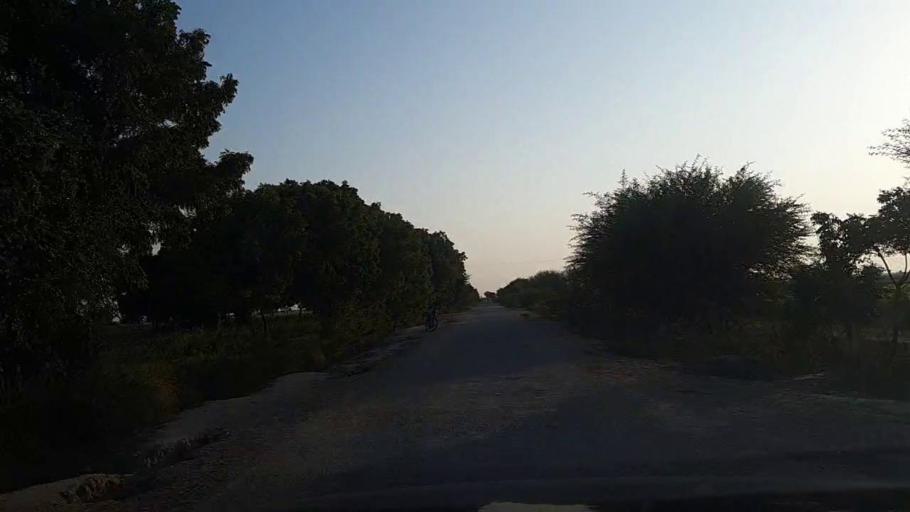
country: PK
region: Sindh
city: Naukot
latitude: 24.8422
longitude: 69.3124
